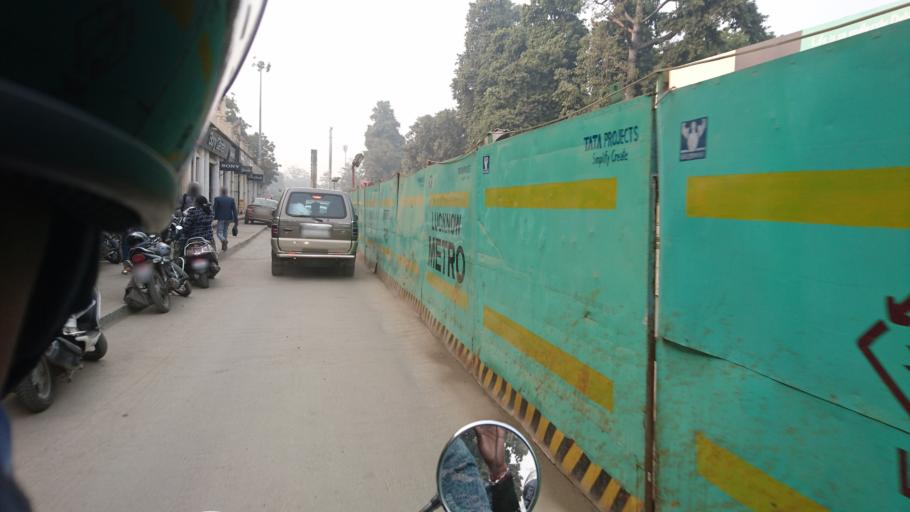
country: IN
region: Uttar Pradesh
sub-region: Lucknow District
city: Lucknow
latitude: 26.8506
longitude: 80.9407
